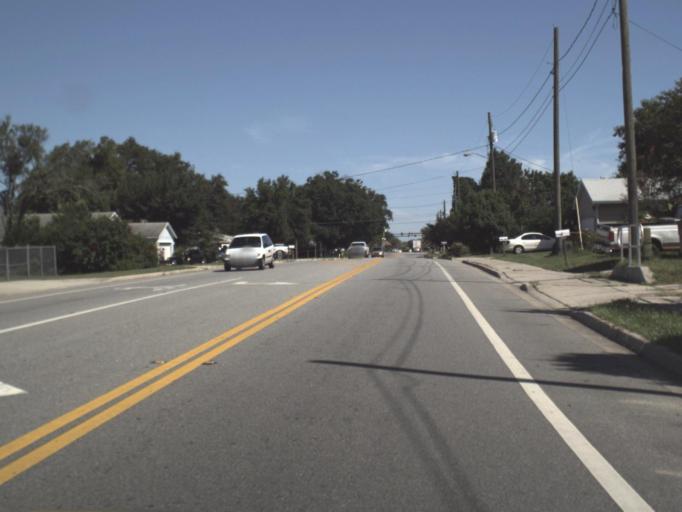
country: US
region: Florida
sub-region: Polk County
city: Auburndale
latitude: 28.0555
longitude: -81.7886
